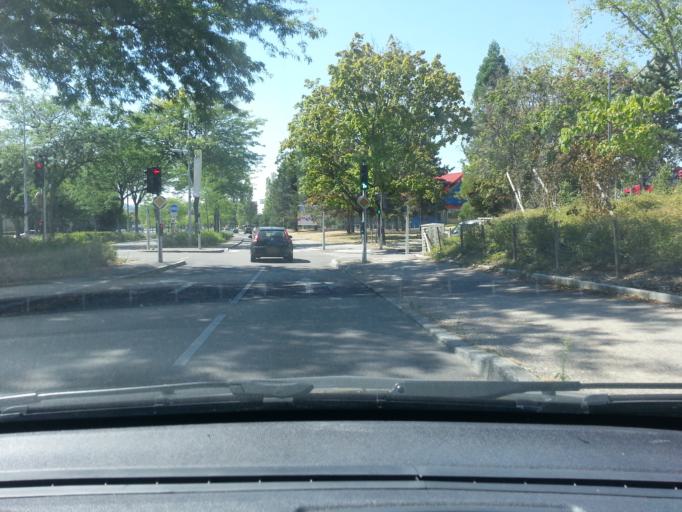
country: FR
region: Bourgogne
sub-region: Departement de la Cote-d'Or
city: Saint-Apollinaire
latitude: 47.3353
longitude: 5.0651
